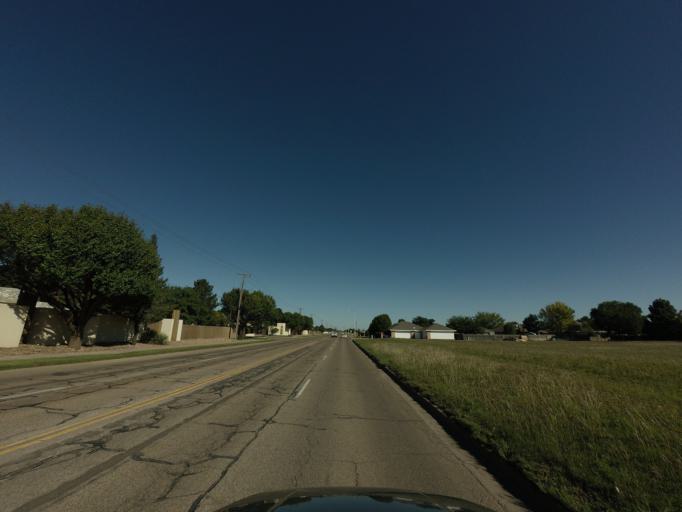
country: US
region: New Mexico
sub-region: Curry County
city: Clovis
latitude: 34.4278
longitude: -103.1785
